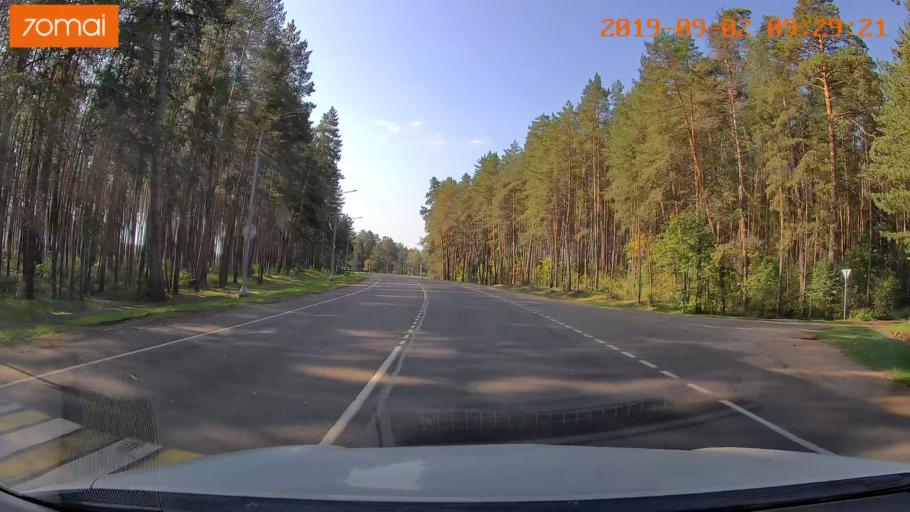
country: RU
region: Kaluga
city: Yukhnov
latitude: 54.7421
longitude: 35.2147
